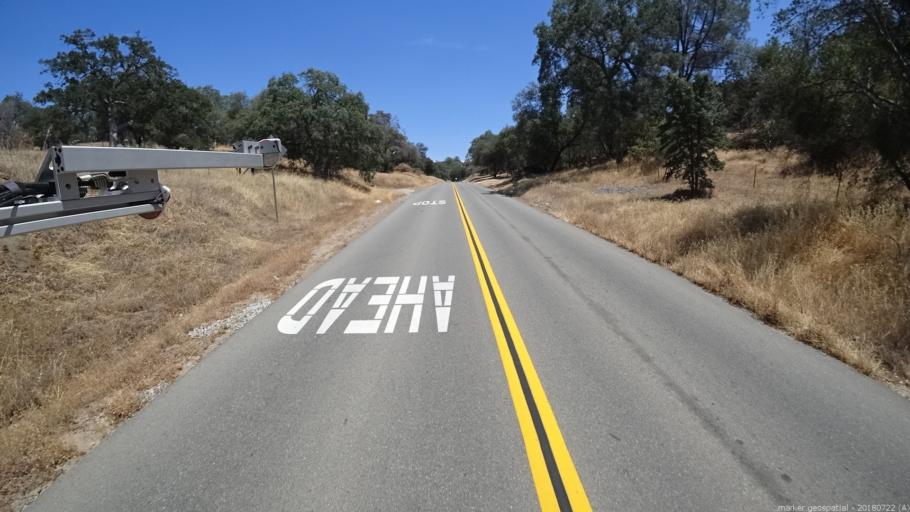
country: US
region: California
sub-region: Madera County
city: Coarsegold
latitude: 37.2314
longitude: -119.7404
